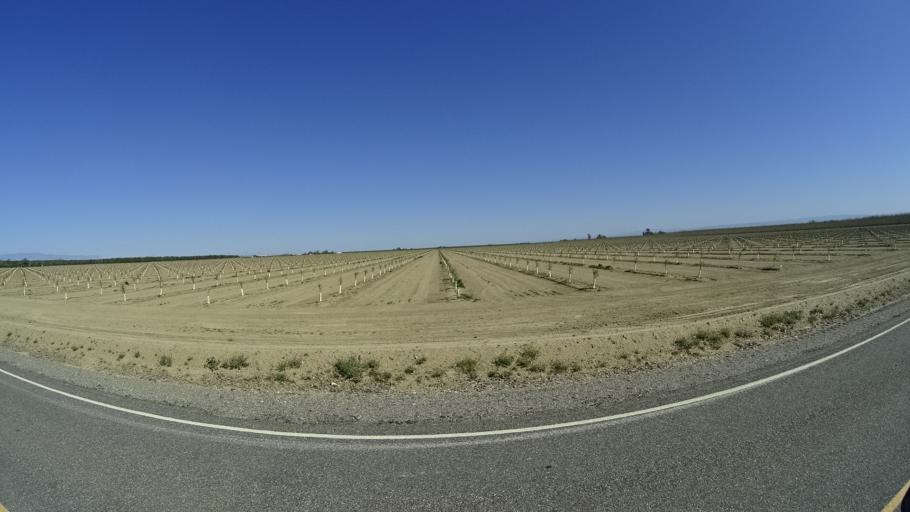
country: US
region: California
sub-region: Glenn County
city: Willows
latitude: 39.6236
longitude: -122.1185
